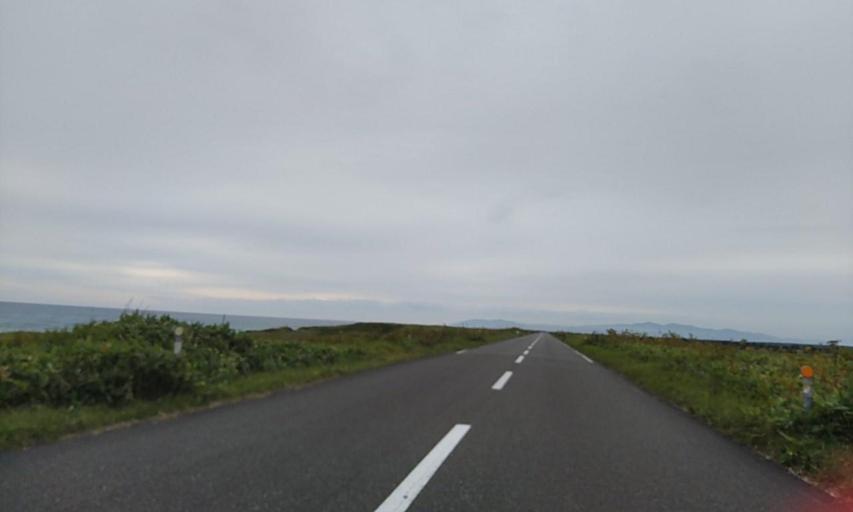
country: JP
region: Hokkaido
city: Makubetsu
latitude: 45.2685
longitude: 142.2387
